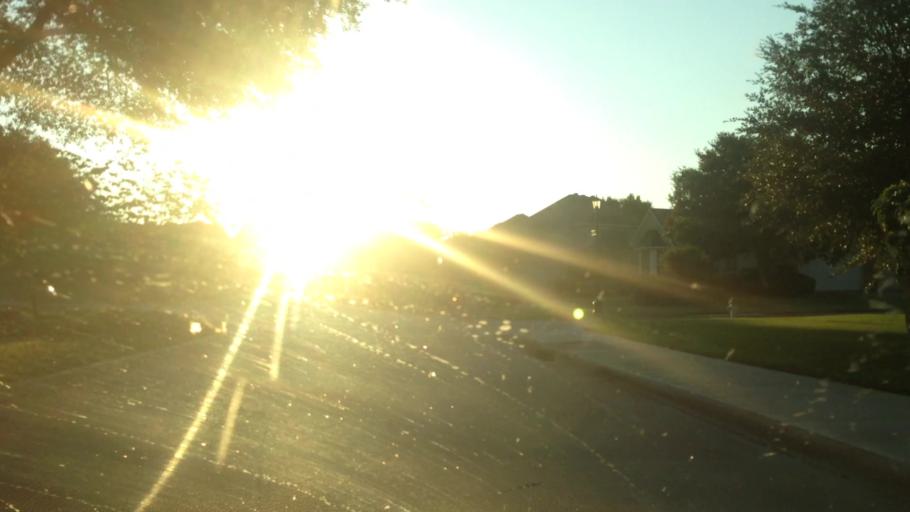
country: US
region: Texas
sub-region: Tarrant County
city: Southlake
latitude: 32.9365
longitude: -97.1332
